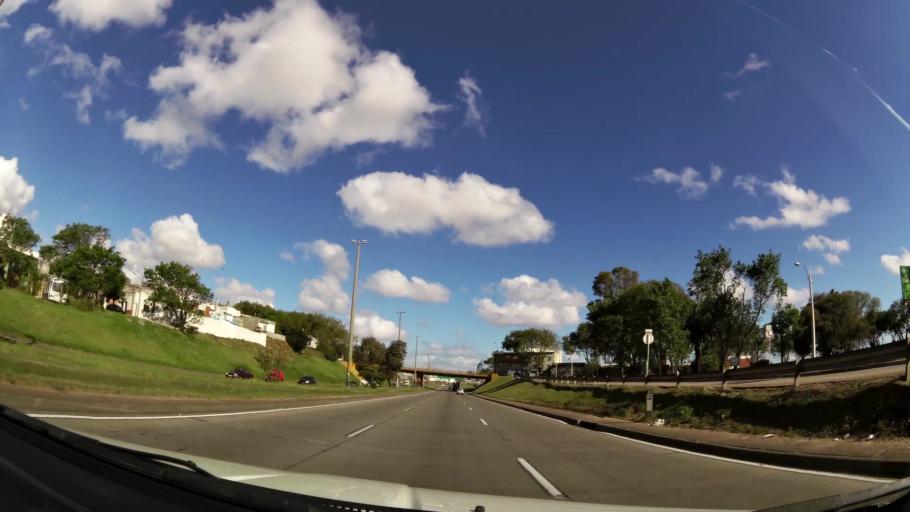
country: UY
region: Montevideo
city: Montevideo
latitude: -34.8717
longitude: -56.2176
